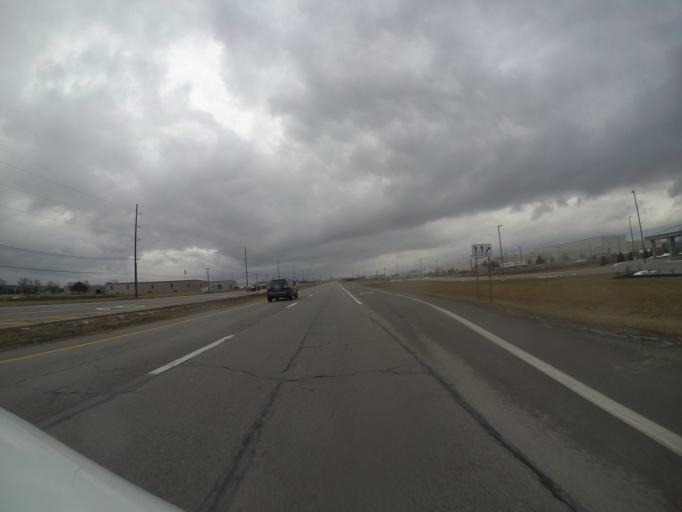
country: US
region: Ohio
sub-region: Wood County
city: Walbridge
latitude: 41.5639
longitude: -83.5386
